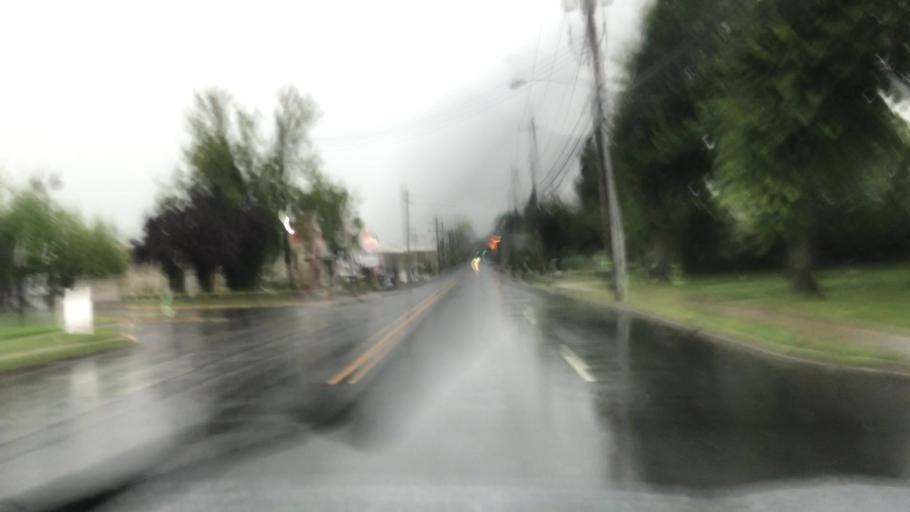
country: US
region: New Jersey
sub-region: Bergen County
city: Closter
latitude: 40.9697
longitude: -73.9534
